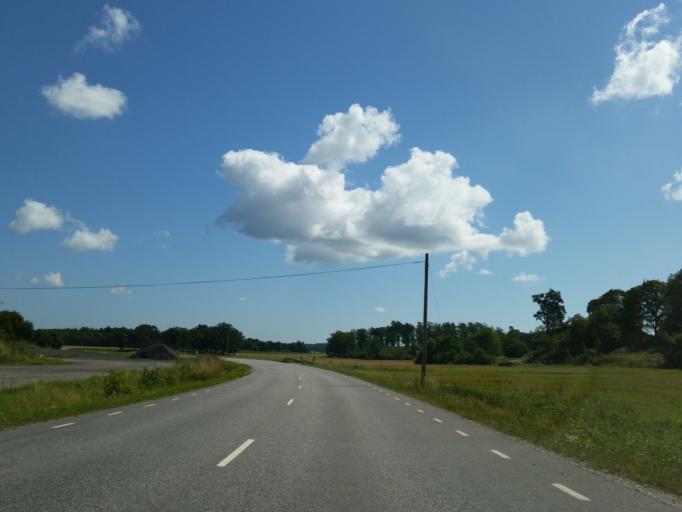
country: SE
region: Soedermanland
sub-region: Trosa Kommun
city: Vagnharad
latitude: 59.0244
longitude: 17.5616
